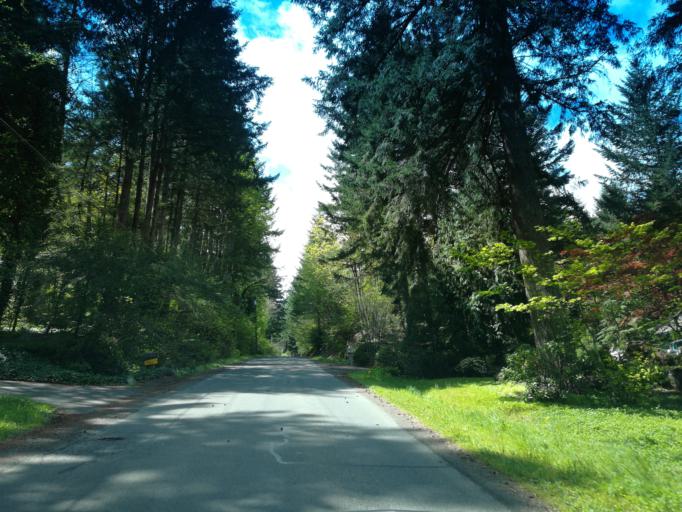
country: US
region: Oregon
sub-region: Clackamas County
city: Damascus
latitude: 45.4430
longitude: -122.4573
